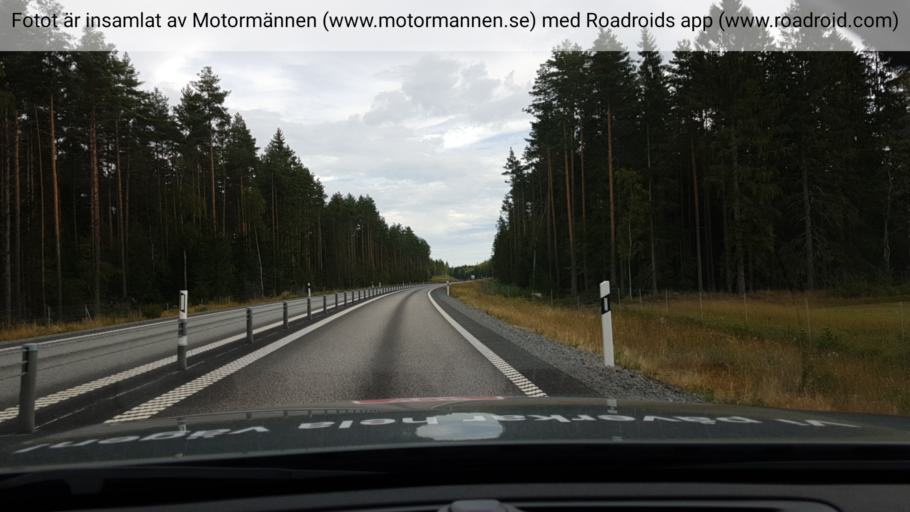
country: SE
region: Uppsala
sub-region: Heby Kommun
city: Heby
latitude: 60.0434
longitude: 16.8756
